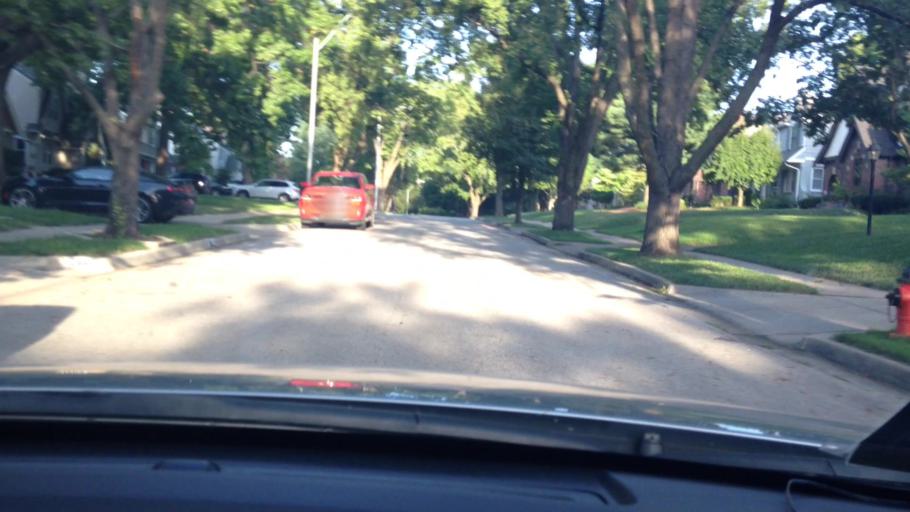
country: US
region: Kansas
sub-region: Johnson County
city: Mission Hills
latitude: 38.9993
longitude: -94.6066
